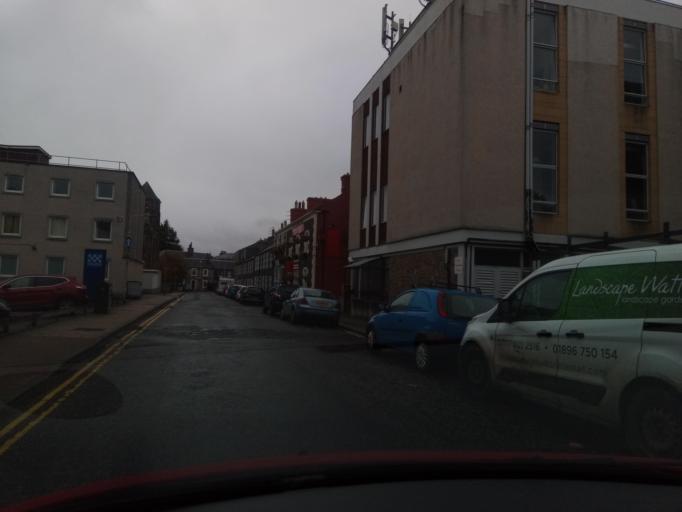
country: GB
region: Scotland
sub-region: The Scottish Borders
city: Galashiels
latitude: 55.6187
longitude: -2.8107
